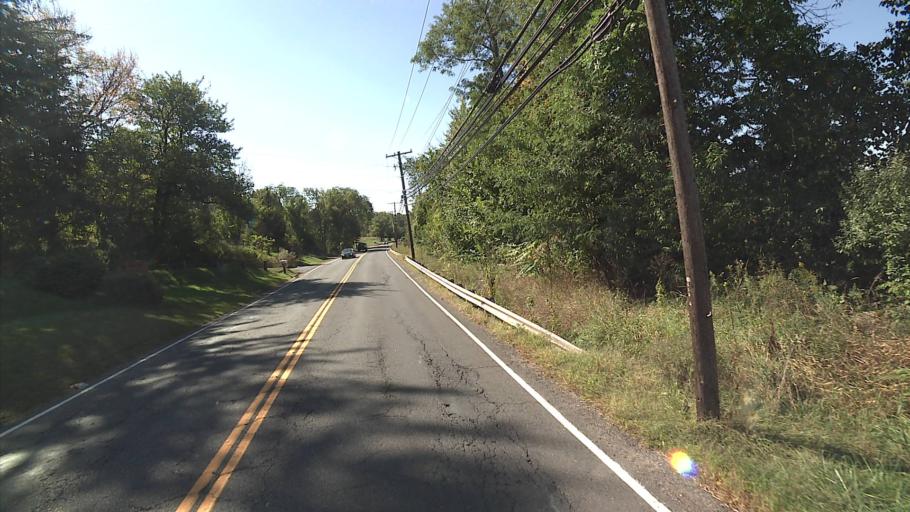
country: US
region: Connecticut
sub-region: Tolland County
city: Ellington
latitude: 41.9073
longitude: -72.4555
